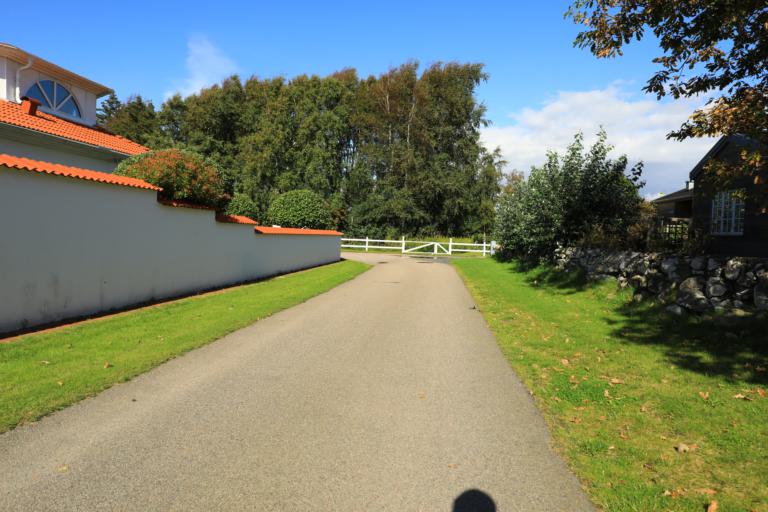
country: SE
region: Halland
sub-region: Varbergs Kommun
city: Traslovslage
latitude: 57.0763
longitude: 12.2670
